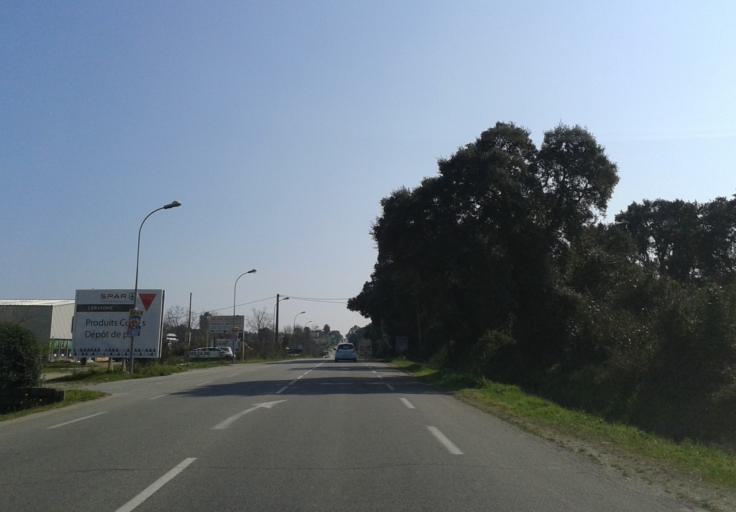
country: FR
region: Corsica
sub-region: Departement de la Haute-Corse
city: Cervione
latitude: 42.3304
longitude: 9.5374
